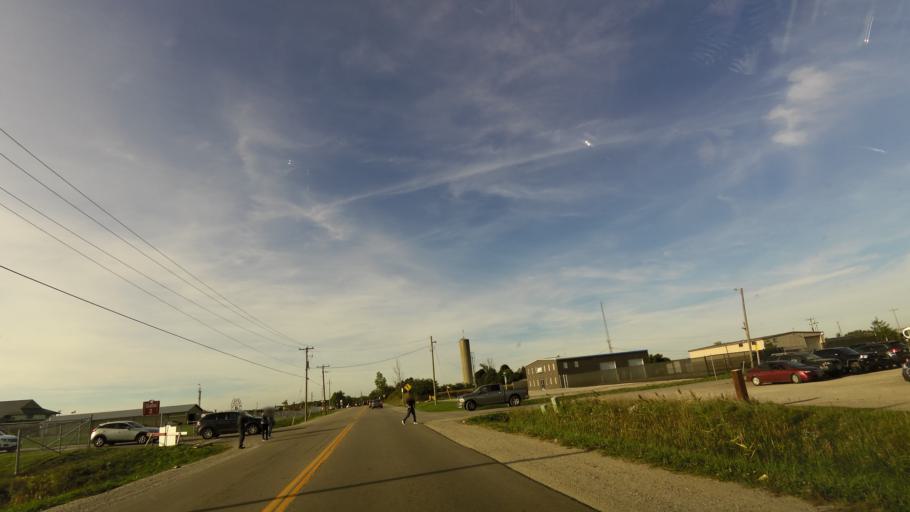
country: CA
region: Ontario
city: Ancaster
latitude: 43.1871
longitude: -80.0399
